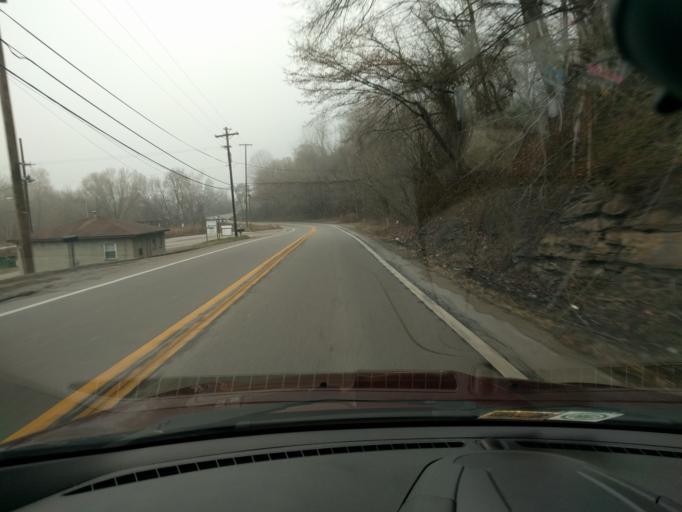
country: US
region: West Virginia
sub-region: Kanawha County
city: Chesapeake
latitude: 38.2051
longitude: -81.4756
